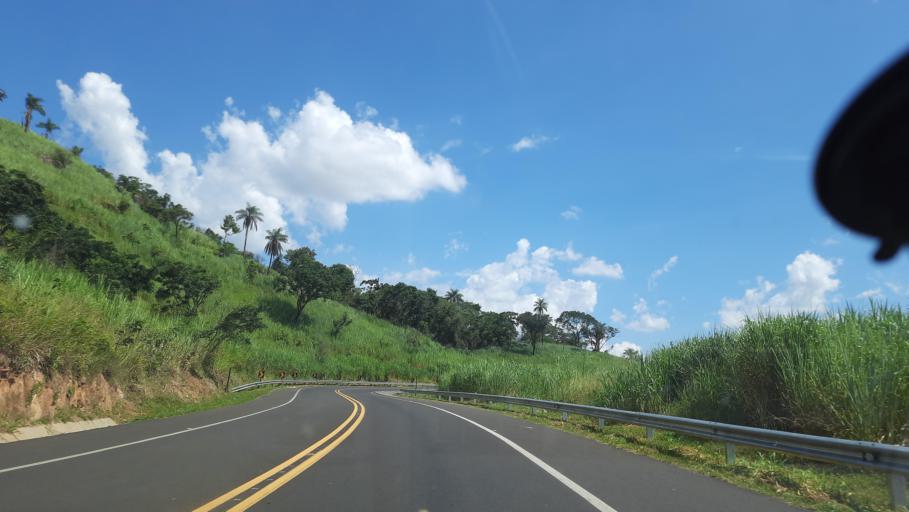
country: BR
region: Sao Paulo
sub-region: Sao Jose Do Rio Pardo
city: Sao Jose do Rio Pardo
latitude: -21.6007
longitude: -46.9377
